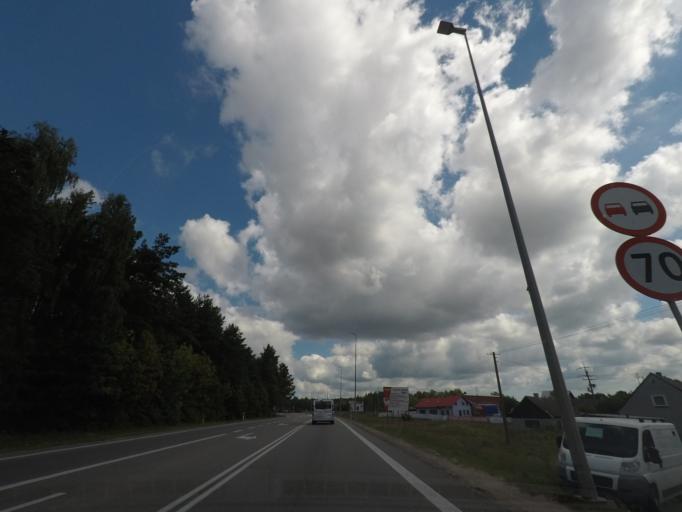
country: PL
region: Pomeranian Voivodeship
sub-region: Powiat wejherowski
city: Luzino
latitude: 54.5855
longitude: 18.1113
